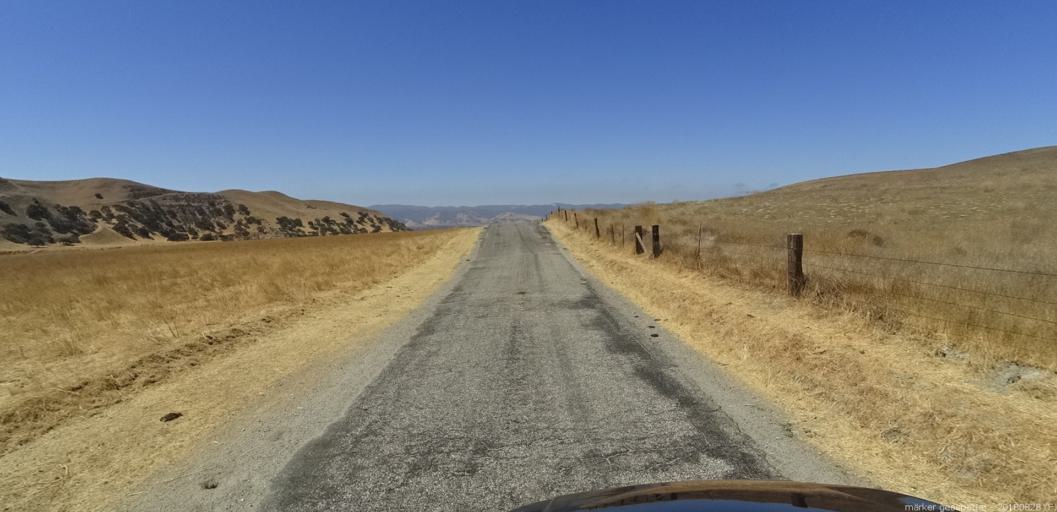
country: US
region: California
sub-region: San Luis Obispo County
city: Lake Nacimiento
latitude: 36.0325
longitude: -120.8547
